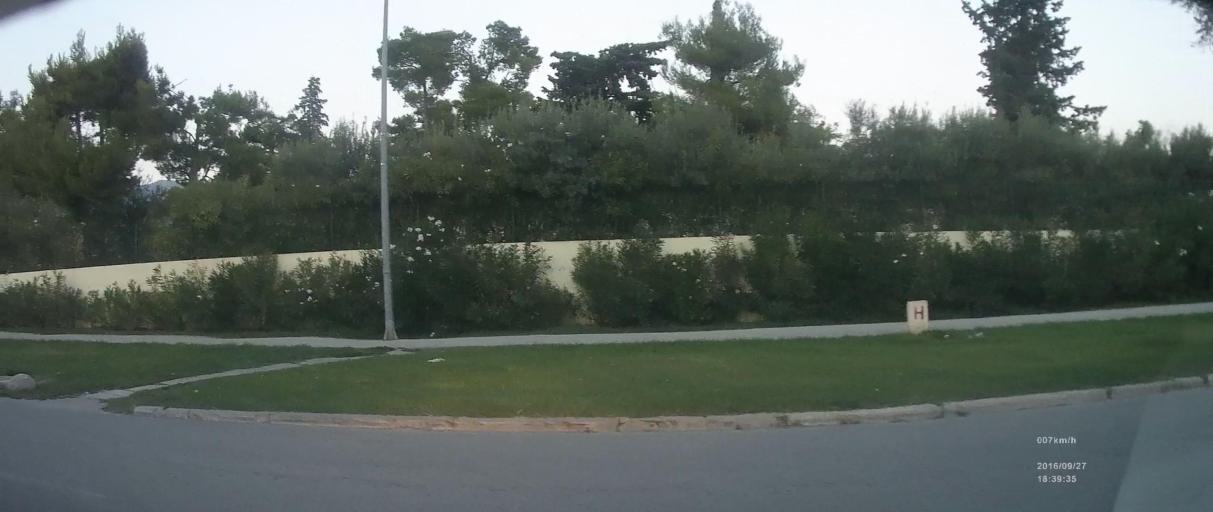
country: HR
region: Splitsko-Dalmatinska
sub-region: Grad Split
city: Stobrec
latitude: 43.5035
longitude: 16.5259
